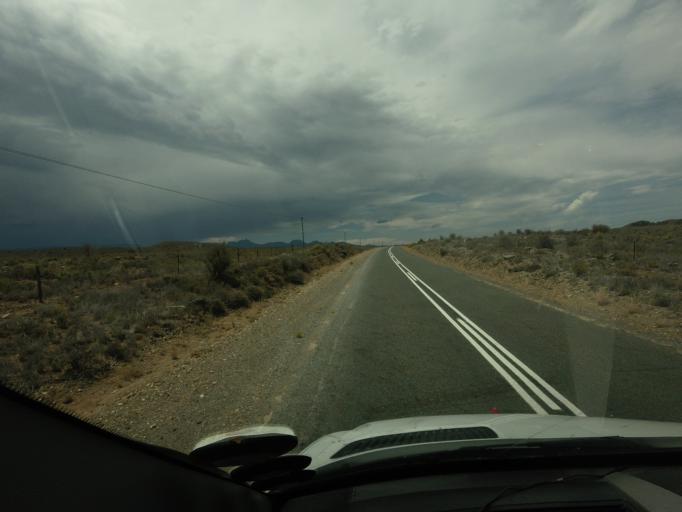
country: ZA
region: Western Cape
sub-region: Eden District Municipality
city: Ladismith
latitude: -33.6067
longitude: 21.0706
